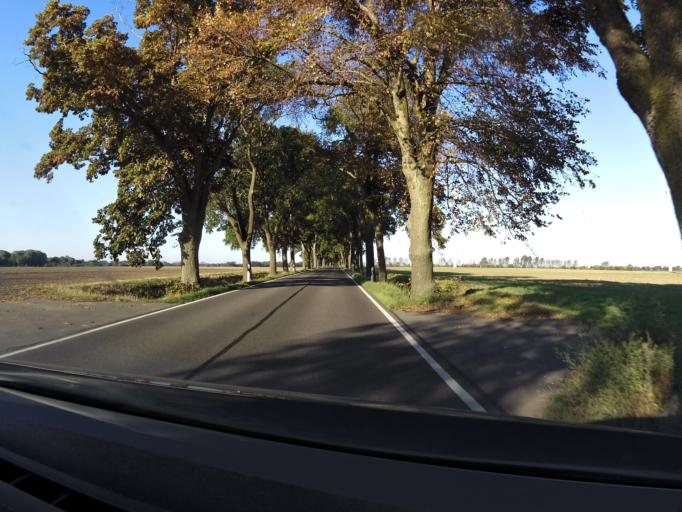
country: DE
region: Mecklenburg-Vorpommern
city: Alt-Sanitz
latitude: 53.8330
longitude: 13.5653
